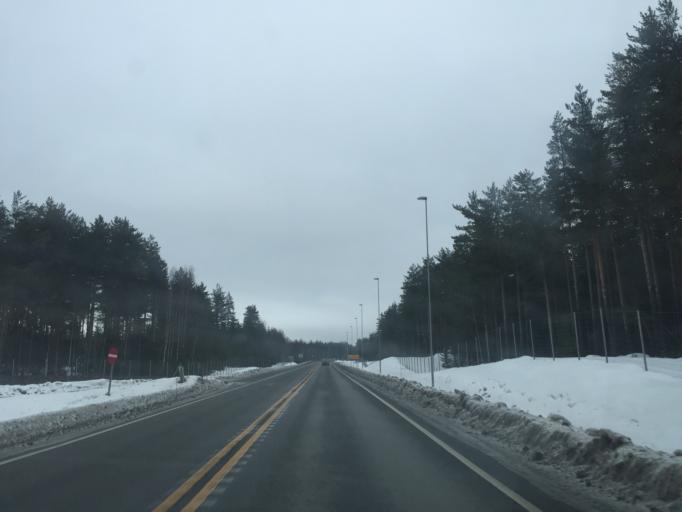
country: NO
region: Hedmark
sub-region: Stange
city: Stange
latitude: 60.7101
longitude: 11.2802
